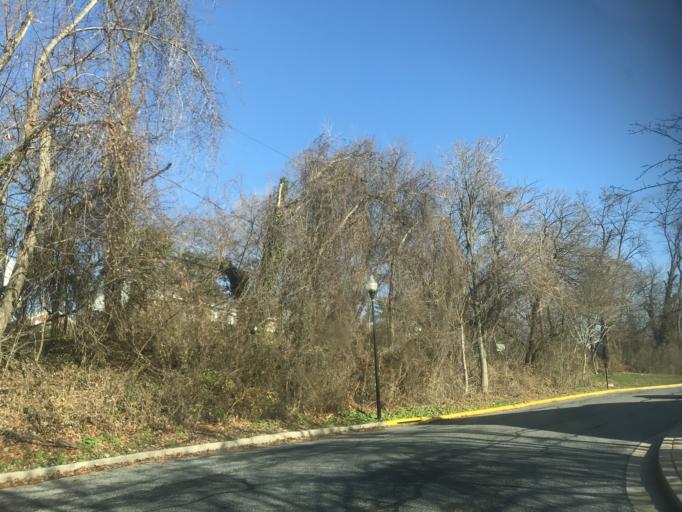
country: US
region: Maryland
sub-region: Baltimore County
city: Hampton
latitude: 39.4048
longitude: -76.5785
